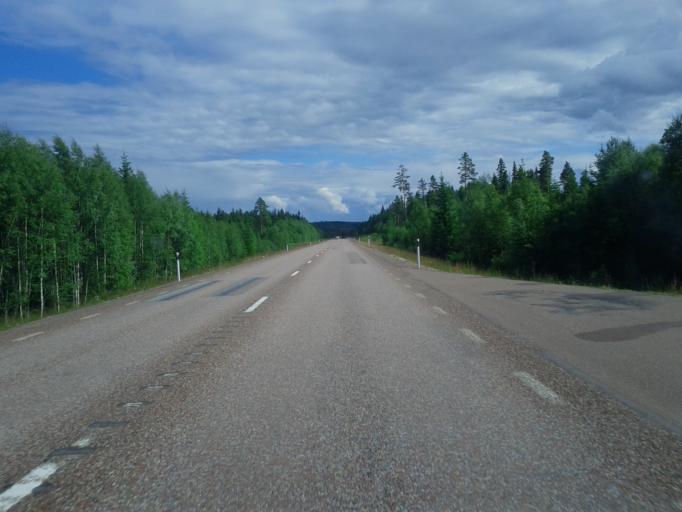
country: SE
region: Dalarna
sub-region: Rattviks Kommun
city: Raettvik
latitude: 60.8284
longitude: 15.2438
